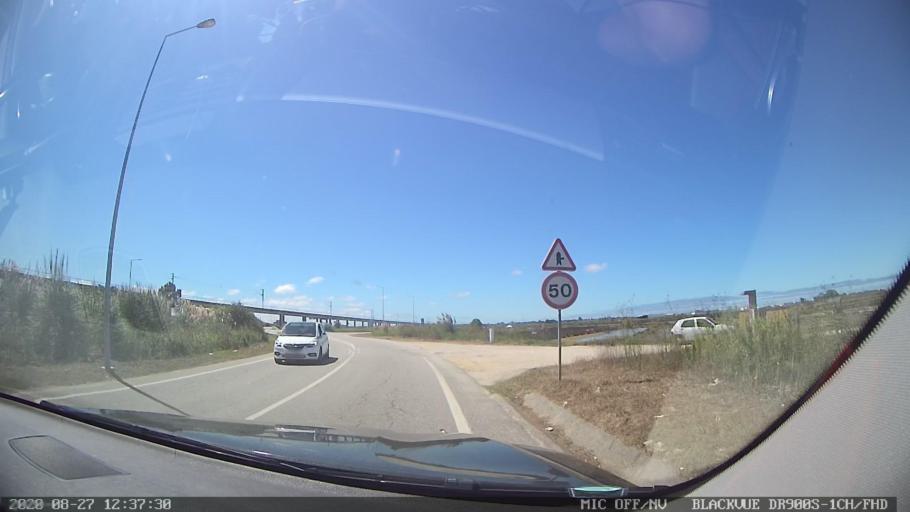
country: PT
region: Aveiro
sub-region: Aveiro
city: Aveiro
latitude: 40.6424
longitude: -8.6628
